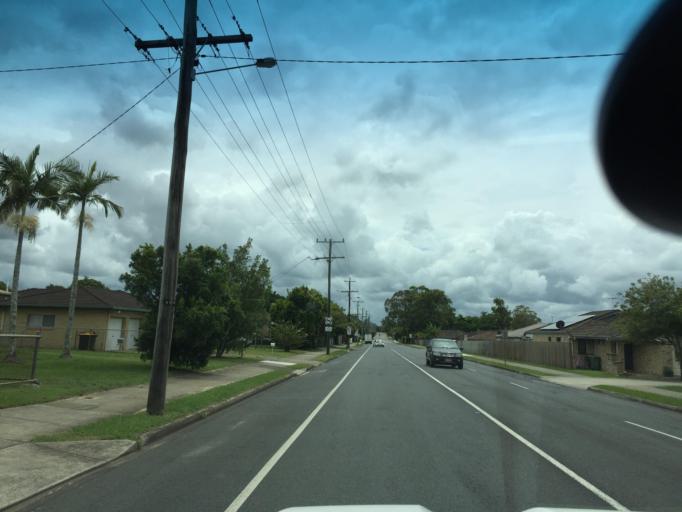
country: AU
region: Queensland
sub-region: Moreton Bay
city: Caboolture
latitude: -27.0760
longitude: 152.9321
